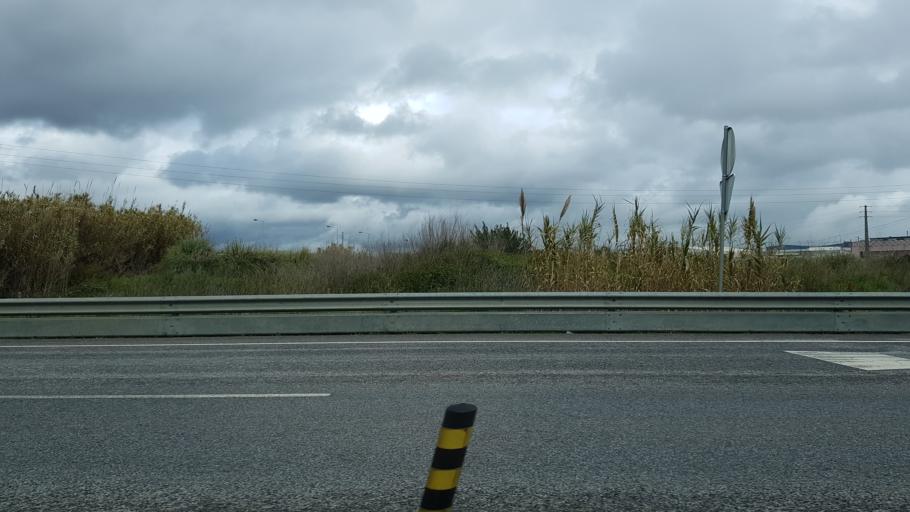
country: PT
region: Lisbon
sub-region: Alenquer
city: Carregado
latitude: 39.0357
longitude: -8.9825
